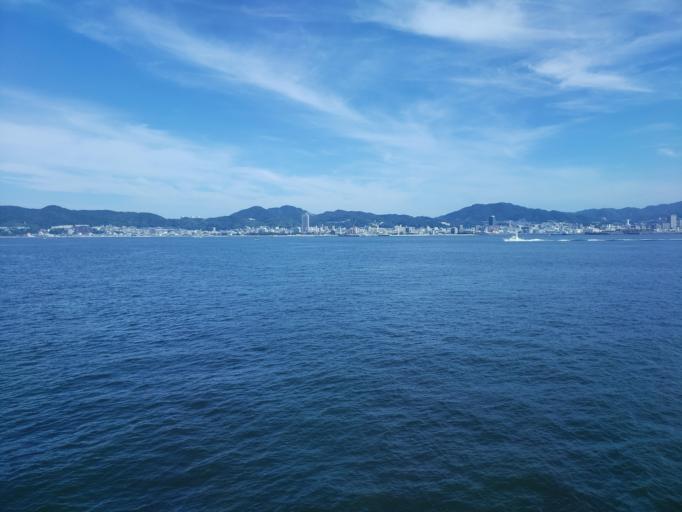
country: JP
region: Hyogo
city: Kobe
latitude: 34.6221
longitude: 135.1410
